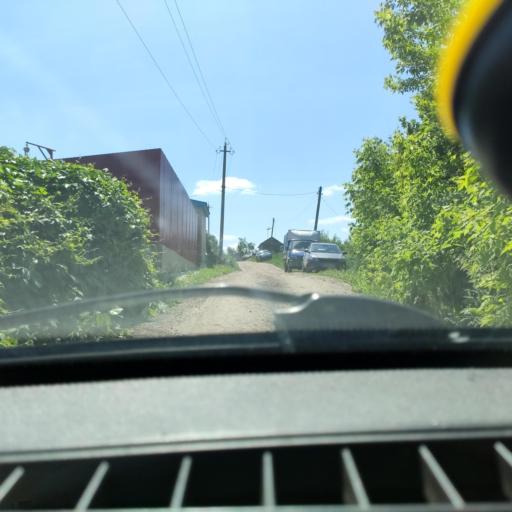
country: RU
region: Samara
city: Zhigulevsk
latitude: 53.3753
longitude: 49.5093
